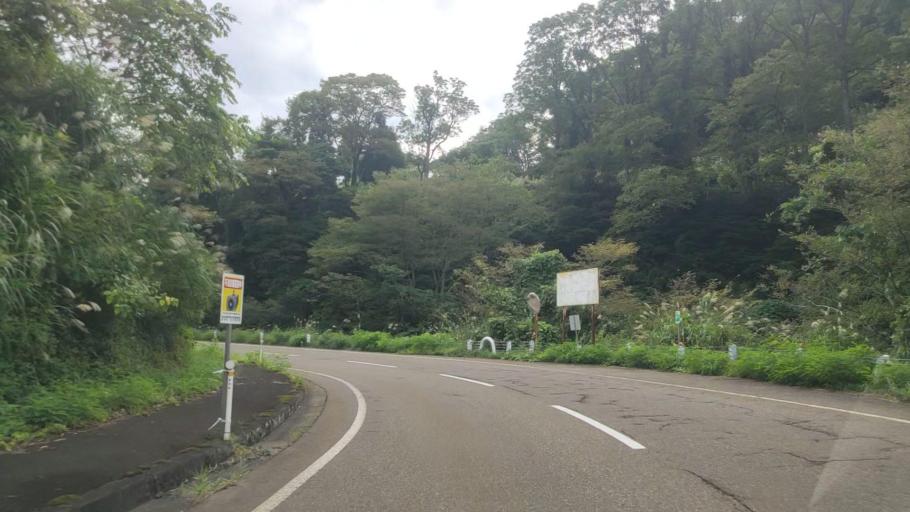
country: JP
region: Niigata
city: Arai
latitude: 36.9347
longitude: 138.2956
